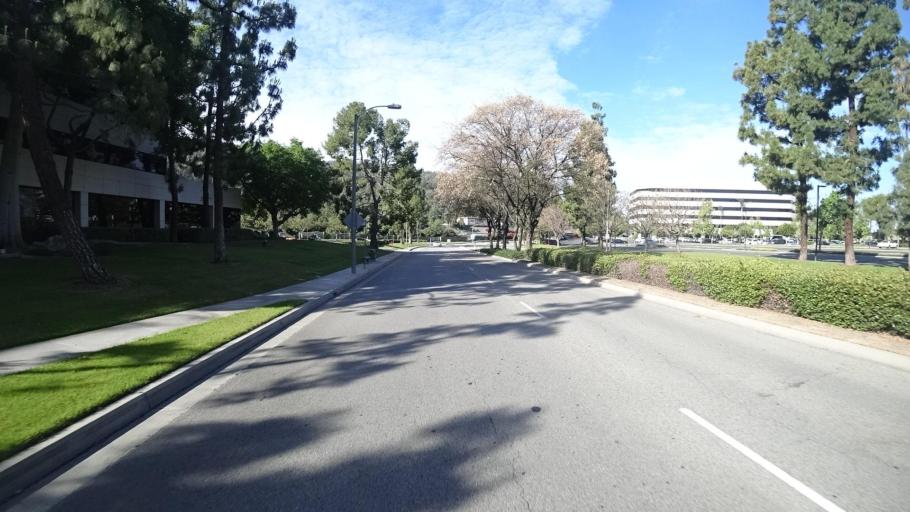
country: US
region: California
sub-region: Los Angeles County
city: Avocado Heights
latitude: 34.0304
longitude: -118.0129
